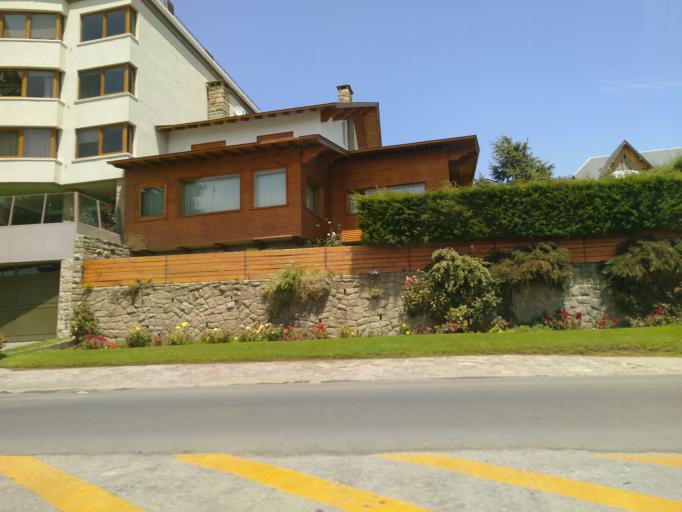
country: AR
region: Rio Negro
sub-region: Departamento de Bariloche
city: San Carlos de Bariloche
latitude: -41.1327
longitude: -71.3092
